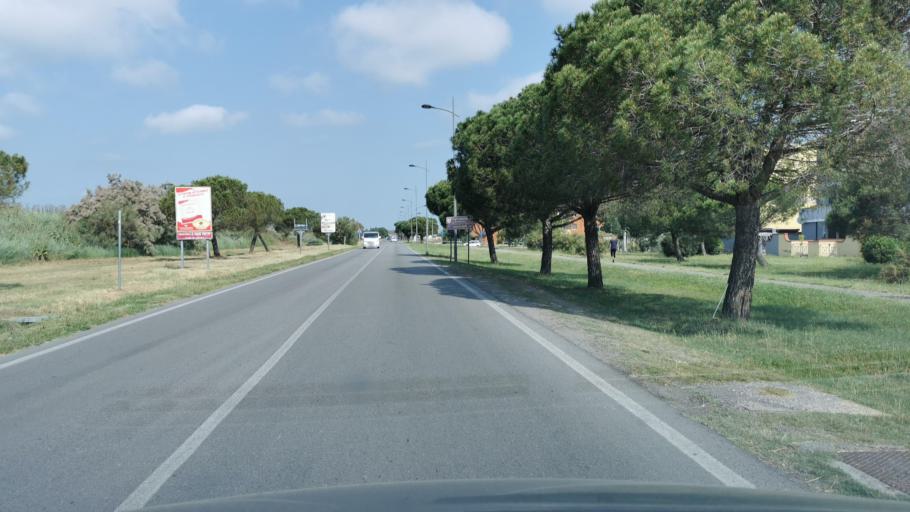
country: IT
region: Emilia-Romagna
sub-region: Provincia di Ferrara
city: Comacchio
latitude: 44.6847
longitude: 12.1957
